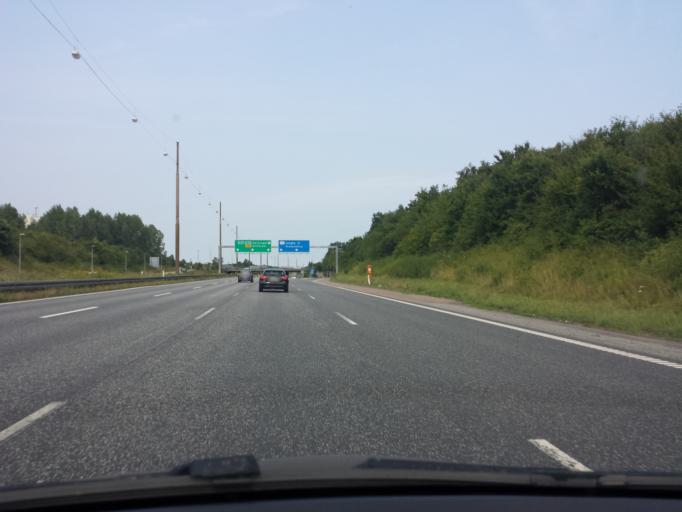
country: DK
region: Capital Region
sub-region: Lyngby-Tarbaek Kommune
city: Kongens Lyngby
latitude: 55.7717
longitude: 12.5239
